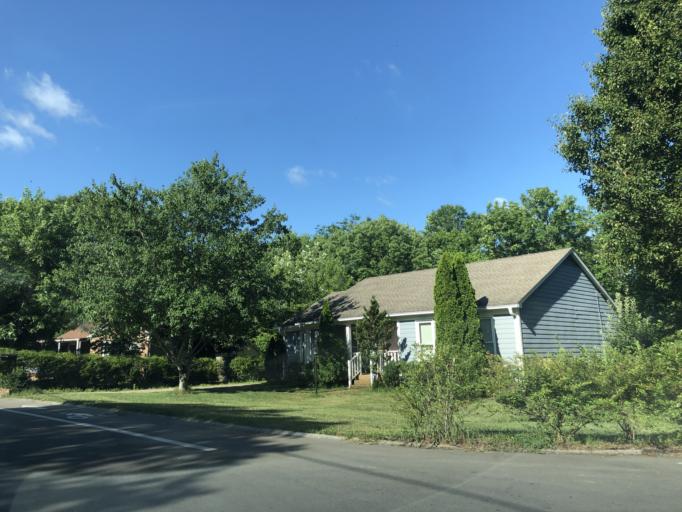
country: US
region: Tennessee
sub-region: Davidson County
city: Belle Meade
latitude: 36.0529
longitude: -86.9458
